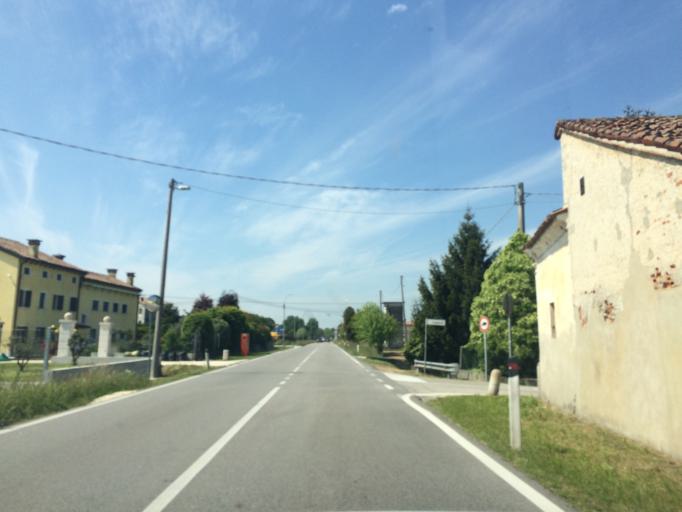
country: IT
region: Veneto
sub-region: Provincia di Padova
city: Cittadella
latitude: 45.6147
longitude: 11.7819
